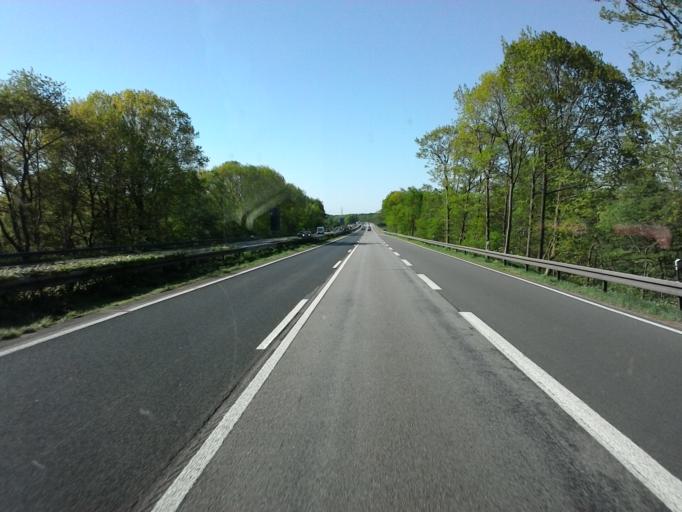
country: DE
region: North Rhine-Westphalia
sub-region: Regierungsbezirk Dusseldorf
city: Hunxe
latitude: 51.6395
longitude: 6.7440
